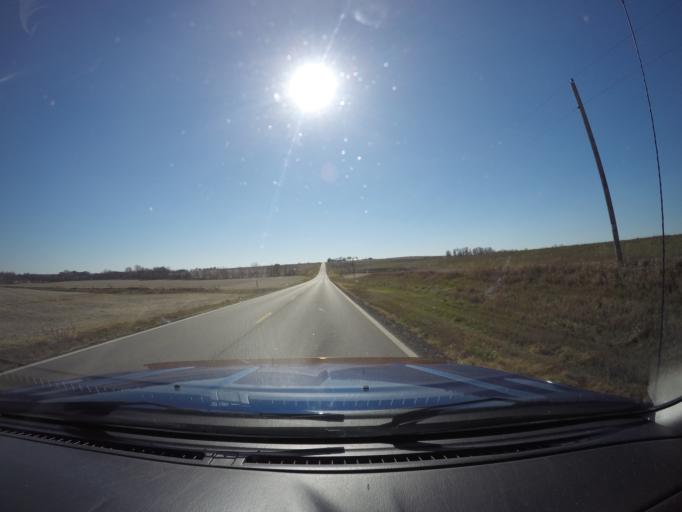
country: US
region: Kansas
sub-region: Nemaha County
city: Seneca
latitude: 39.8531
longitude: -96.2585
